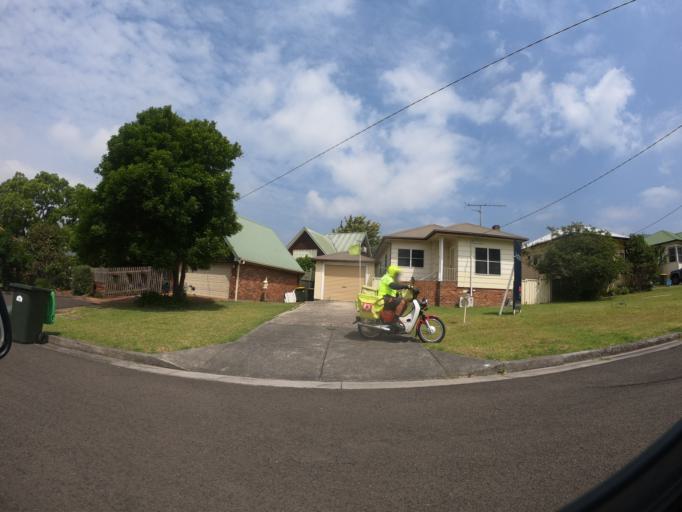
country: AU
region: New South Wales
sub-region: Wollongong
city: Fairy Meadow
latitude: -34.3842
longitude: 150.8867
